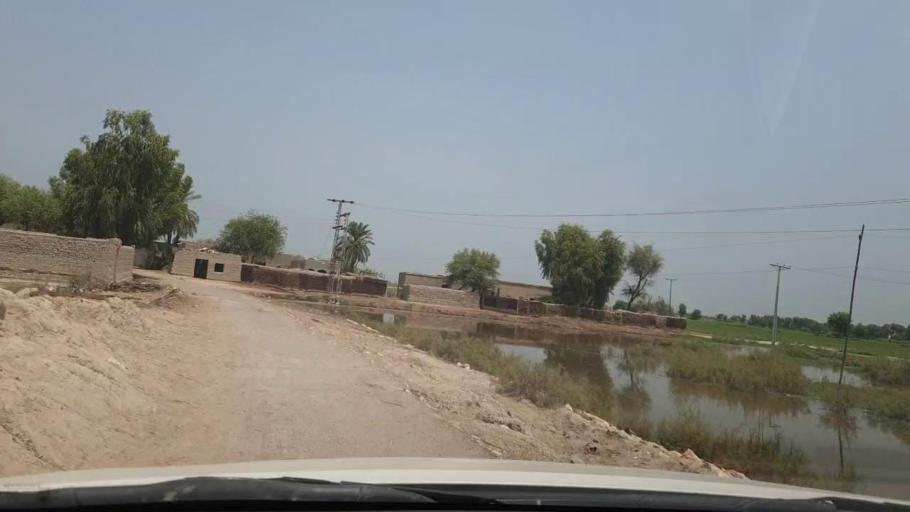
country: PK
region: Sindh
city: Rustam jo Goth
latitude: 28.0166
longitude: 68.7838
